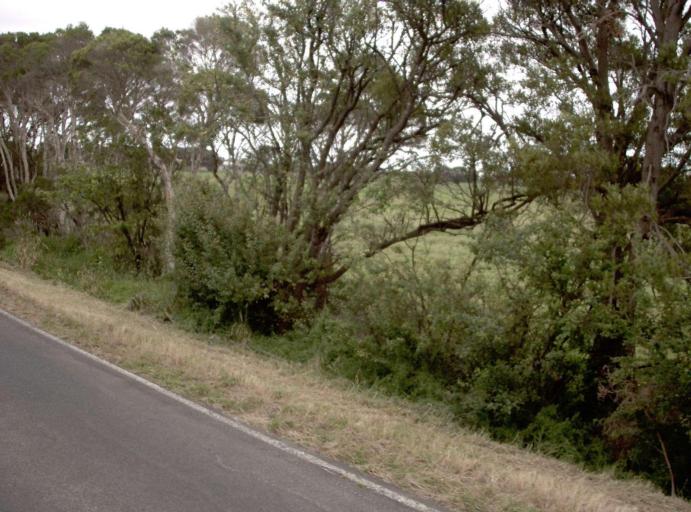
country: AU
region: Victoria
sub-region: Bass Coast
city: North Wonthaggi
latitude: -38.5828
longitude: 145.6221
